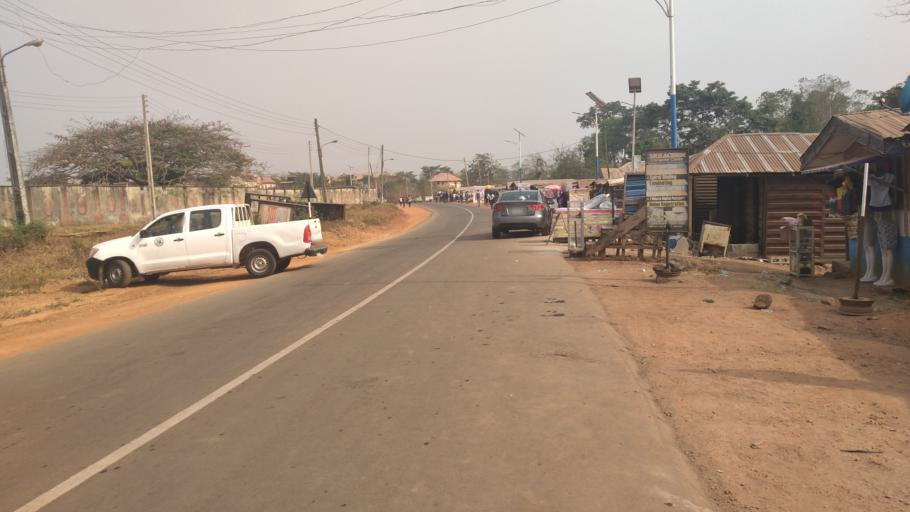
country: NG
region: Ondo
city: Ilare
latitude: 7.3031
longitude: 5.1410
